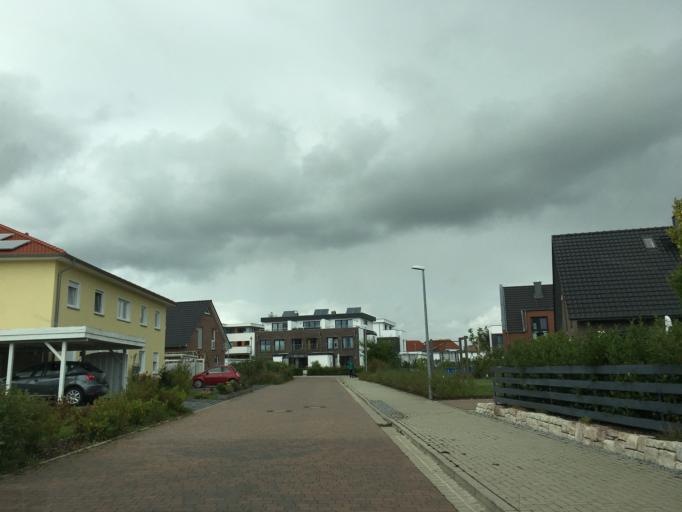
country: DE
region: Lower Saxony
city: Melbeck
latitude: 53.2090
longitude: 10.3759
